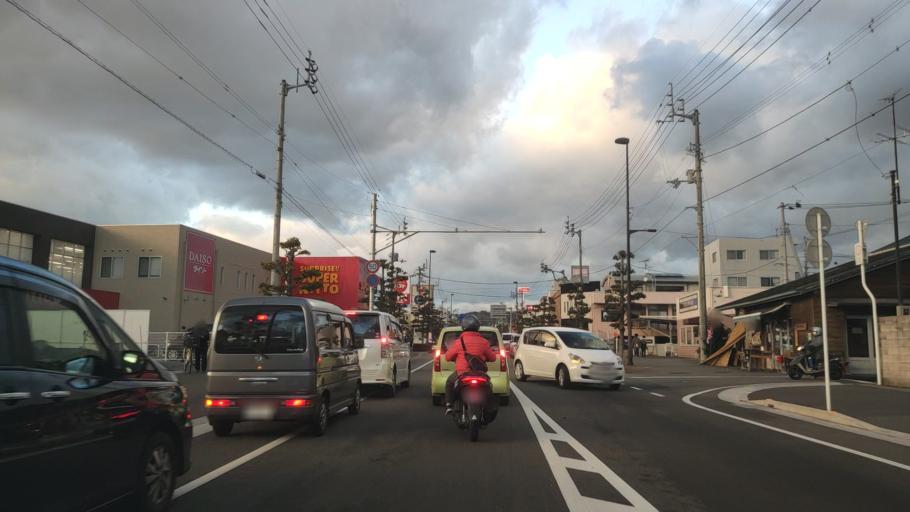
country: JP
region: Ehime
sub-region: Shikoku-chuo Shi
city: Matsuyama
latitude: 33.8306
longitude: 132.7875
